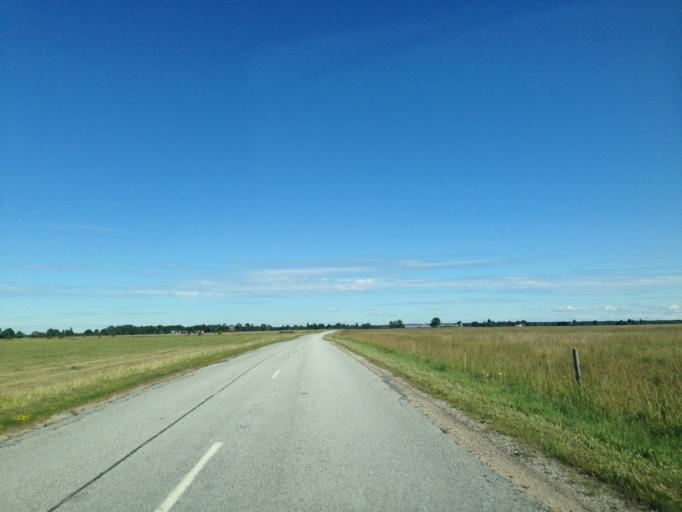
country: EE
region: Harju
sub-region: Kuusalu vald
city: Kuusalu
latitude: 59.4641
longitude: 25.3286
